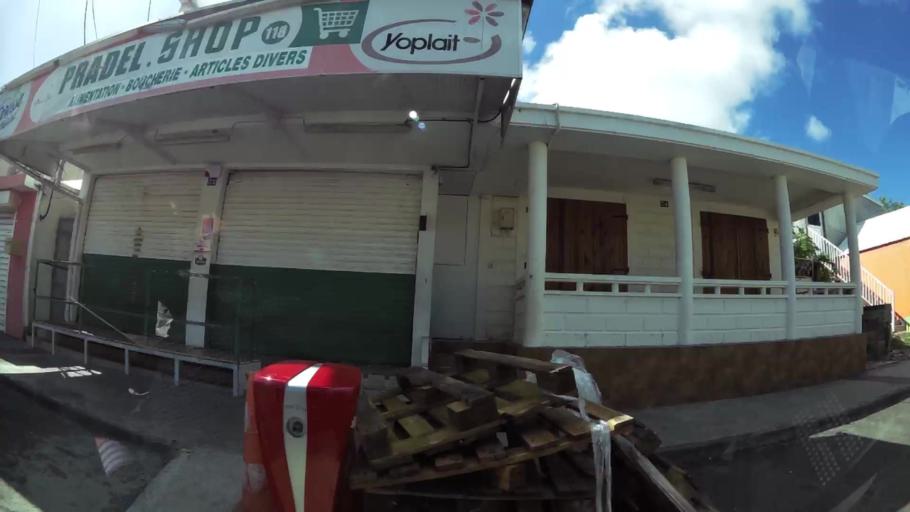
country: GP
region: Guadeloupe
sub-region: Guadeloupe
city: Saint-Francois
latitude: 16.2530
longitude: -61.2746
